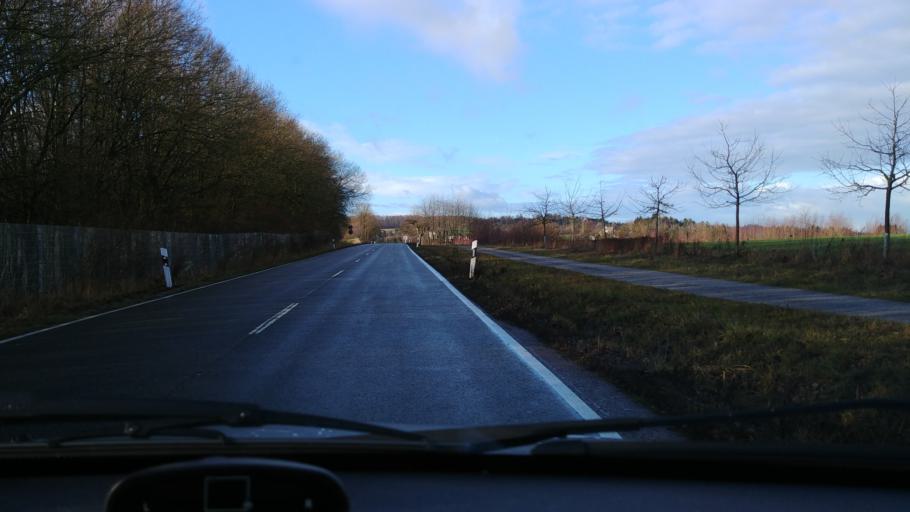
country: DE
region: Hesse
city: Taunusstein
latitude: 50.1818
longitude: 8.1992
